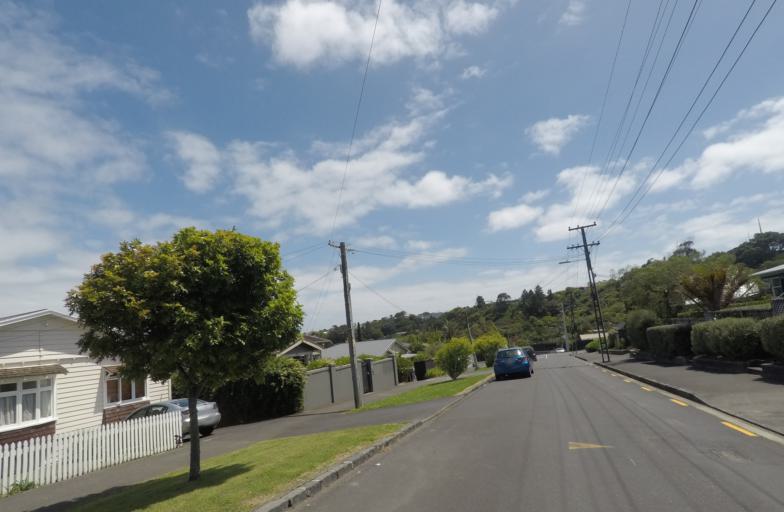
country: NZ
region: Auckland
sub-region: Auckland
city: Auckland
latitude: -36.8703
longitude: 174.7377
